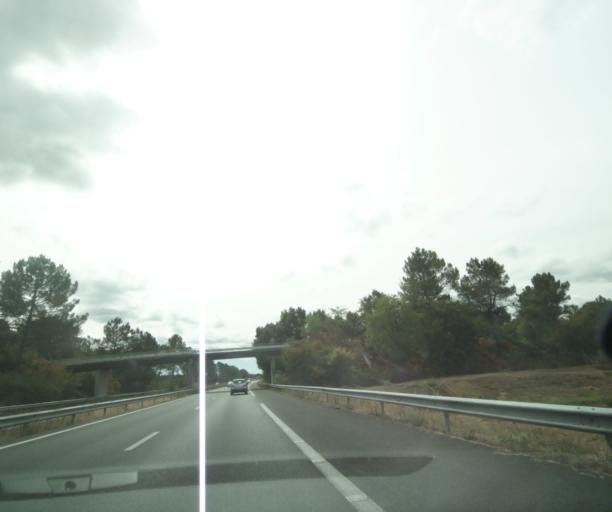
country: FR
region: Aquitaine
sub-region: Departement de la Gironde
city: Reignac
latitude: 45.1990
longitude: -0.4959
